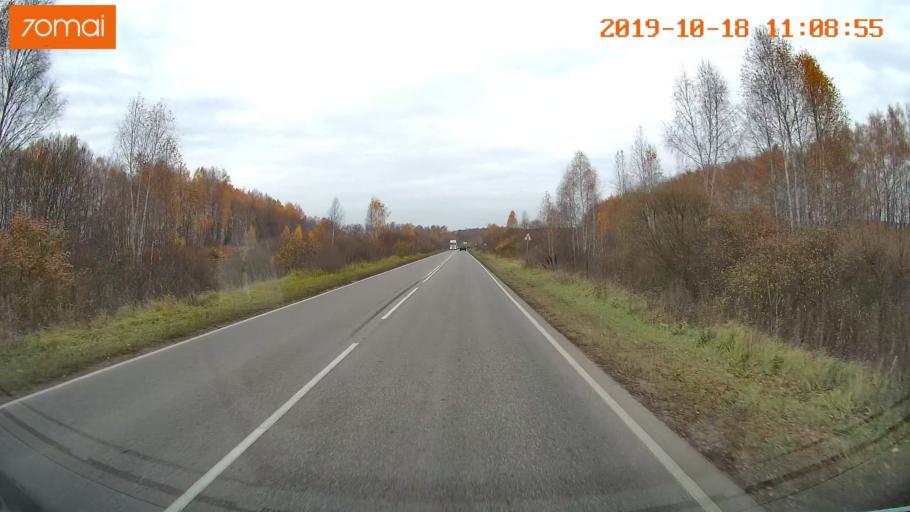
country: RU
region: Tula
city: Kimovsk
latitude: 53.9457
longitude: 38.5340
